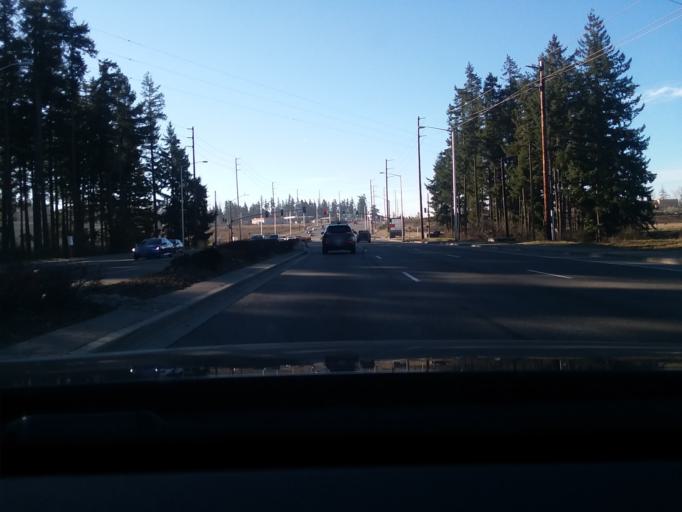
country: US
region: Washington
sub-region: Pierce County
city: Frederickson
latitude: 47.1011
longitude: -122.3573
